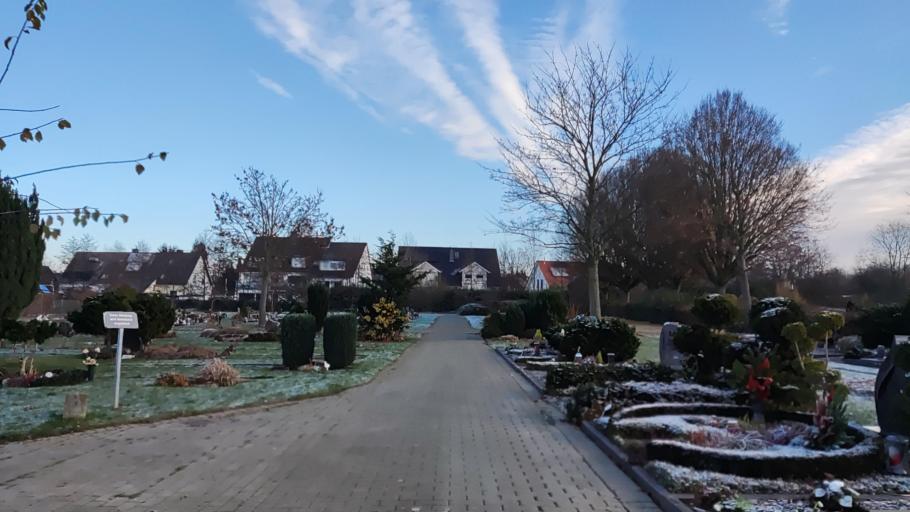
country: DE
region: North Rhine-Westphalia
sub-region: Regierungsbezirk Arnsberg
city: Herne
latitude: 51.5345
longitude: 7.1954
